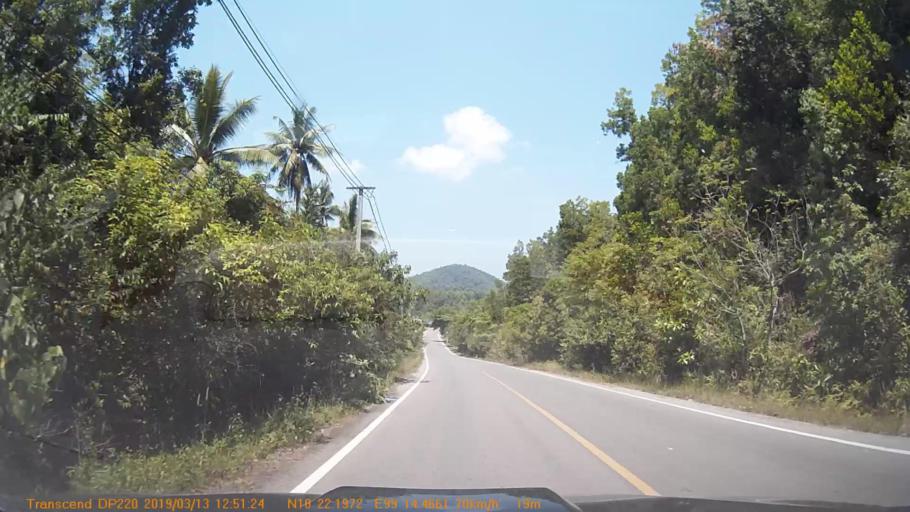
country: TH
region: Chumphon
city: Chumphon
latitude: 10.3705
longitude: 99.2412
